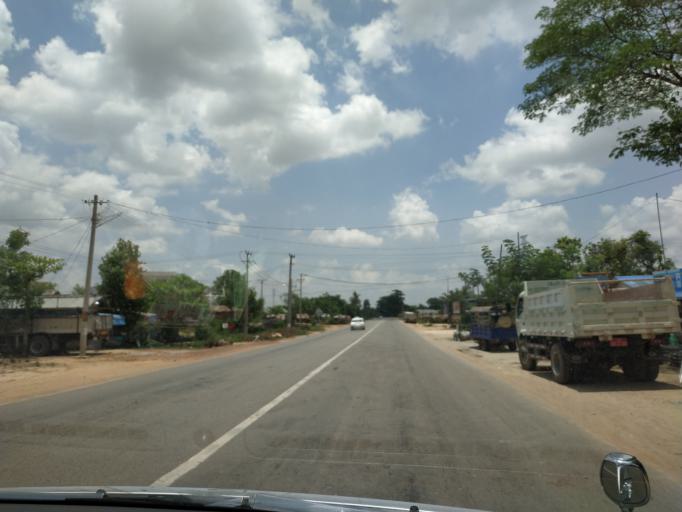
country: MM
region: Bago
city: Bago
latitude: 17.4733
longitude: 96.5390
